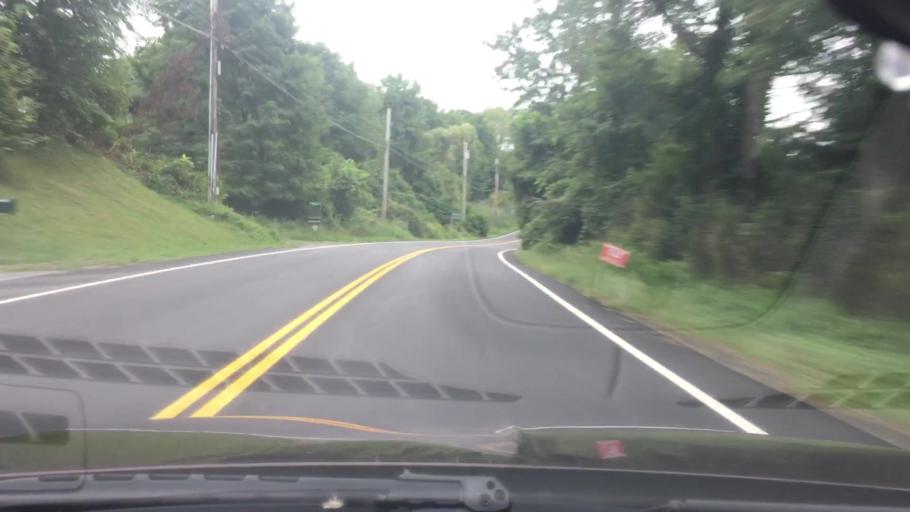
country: US
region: New York
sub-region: Dutchess County
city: Millbrook
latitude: 41.8384
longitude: -73.6104
